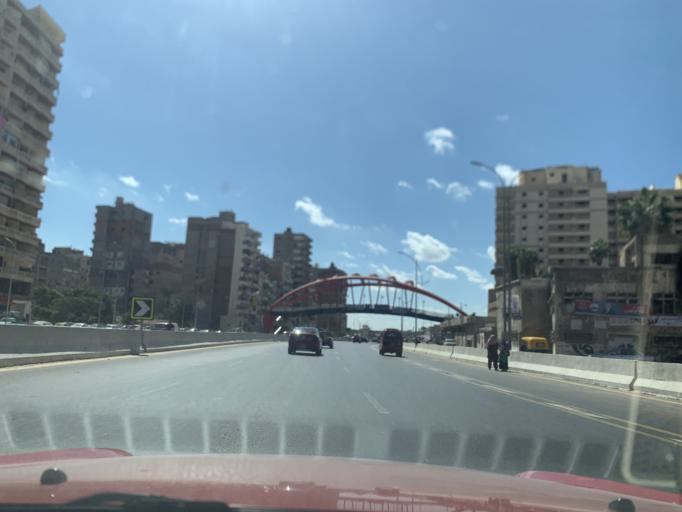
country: EG
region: Alexandria
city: Alexandria
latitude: 31.1947
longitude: 29.9330
